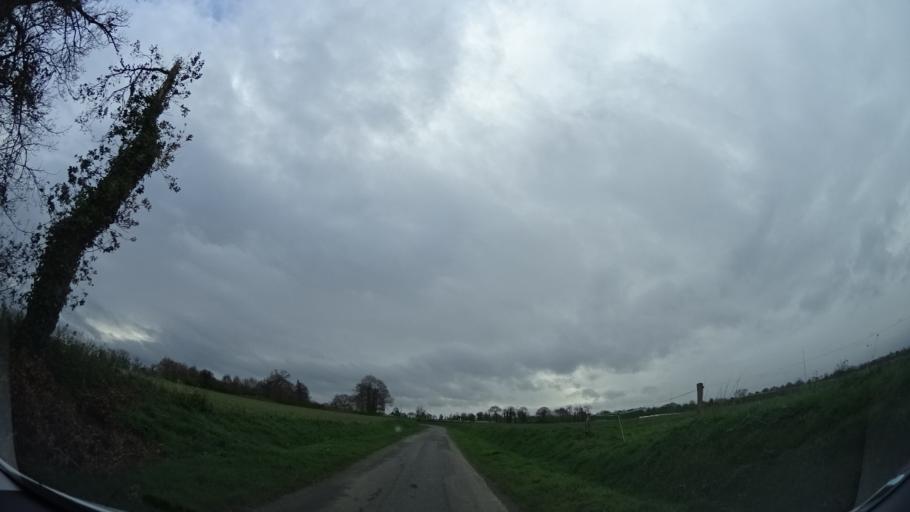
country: FR
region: Brittany
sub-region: Departement des Cotes-d'Armor
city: Evran
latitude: 48.3329
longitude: -1.9490
